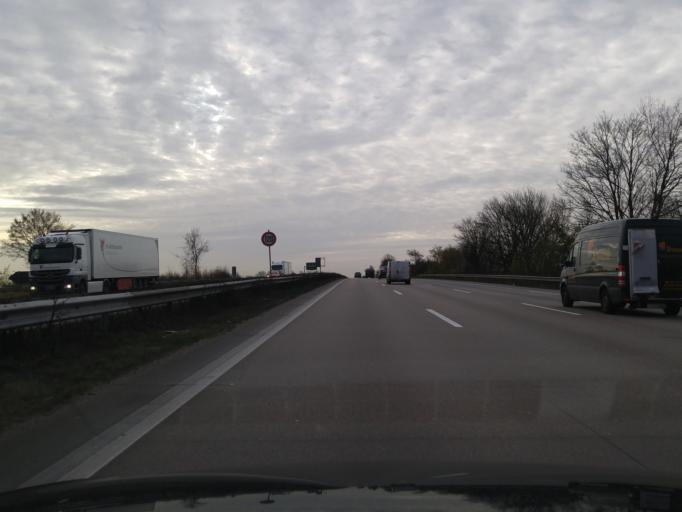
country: DE
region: Schleswig-Holstein
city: Braak
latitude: 53.6144
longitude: 10.2328
